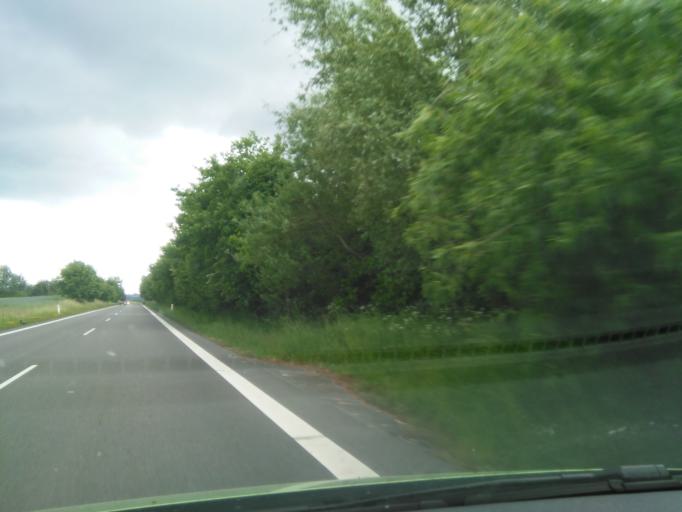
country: DK
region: Capital Region
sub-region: Bornholm Kommune
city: Akirkeby
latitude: 55.2185
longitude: 14.9171
